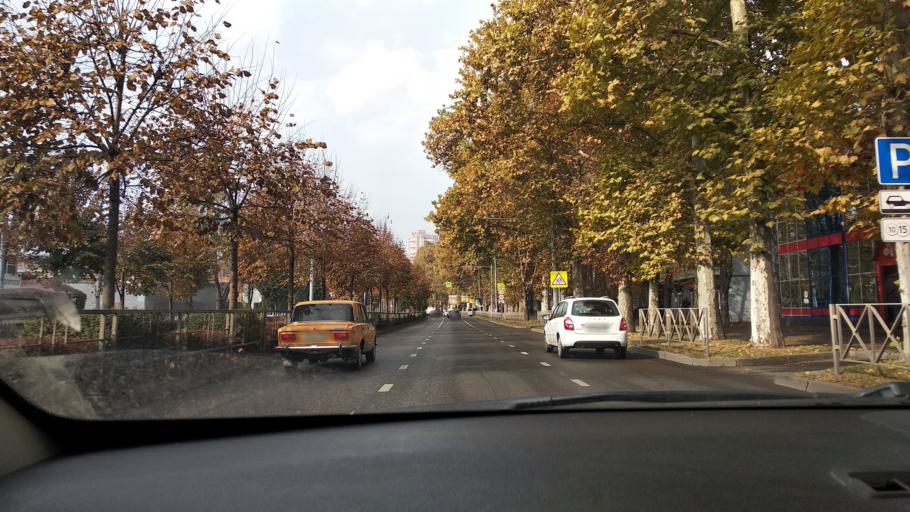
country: RU
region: Krasnodarskiy
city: Krasnodar
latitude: 45.0210
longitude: 39.0215
